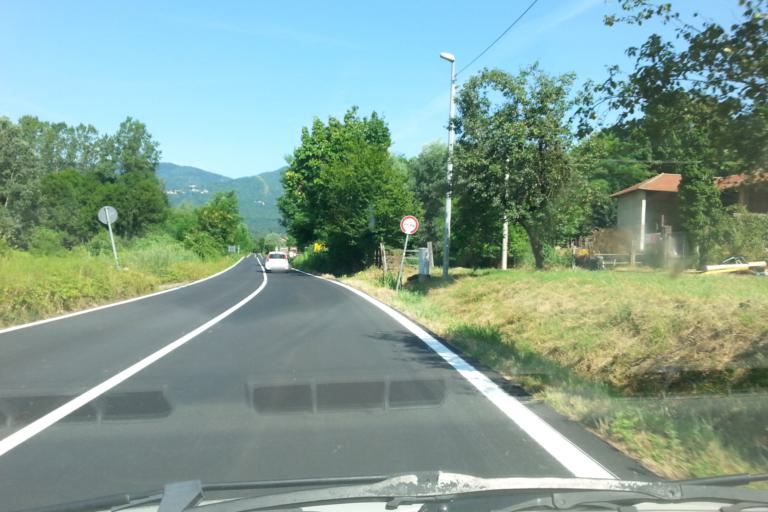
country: IT
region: Piedmont
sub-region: Provincia di Torino
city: Trana
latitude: 45.0493
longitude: 7.4033
